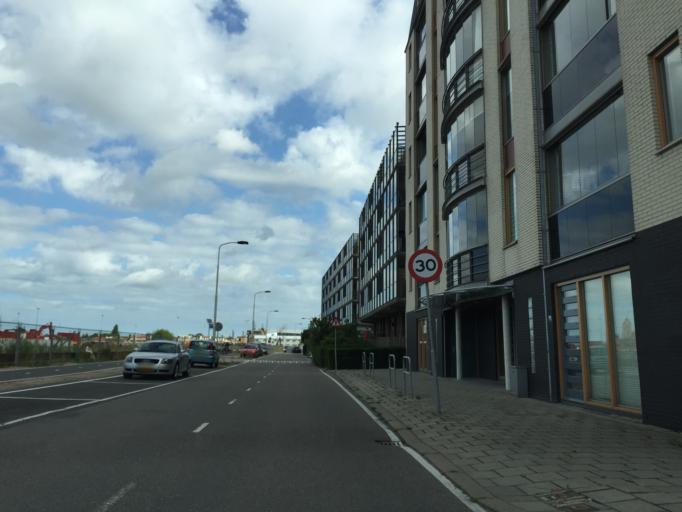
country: NL
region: South Holland
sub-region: Gemeente Delft
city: Delft
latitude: 52.0019
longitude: 4.3592
